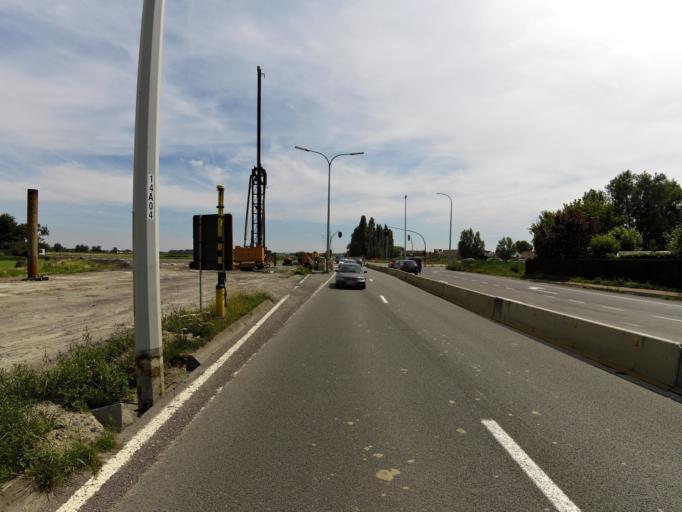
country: BE
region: Flanders
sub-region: Provincie West-Vlaanderen
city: Knokke-Heist
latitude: 51.3153
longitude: 3.3097
